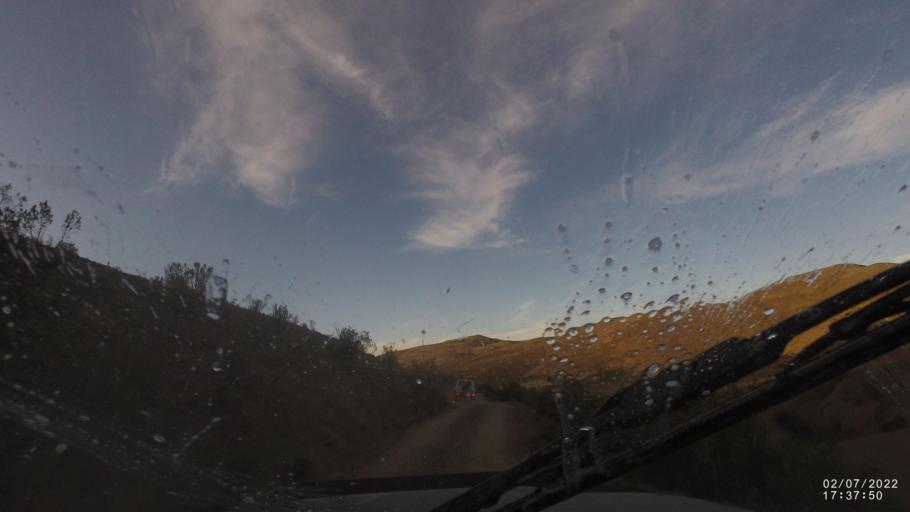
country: BO
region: Cochabamba
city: Irpa Irpa
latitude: -17.8713
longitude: -66.6188
